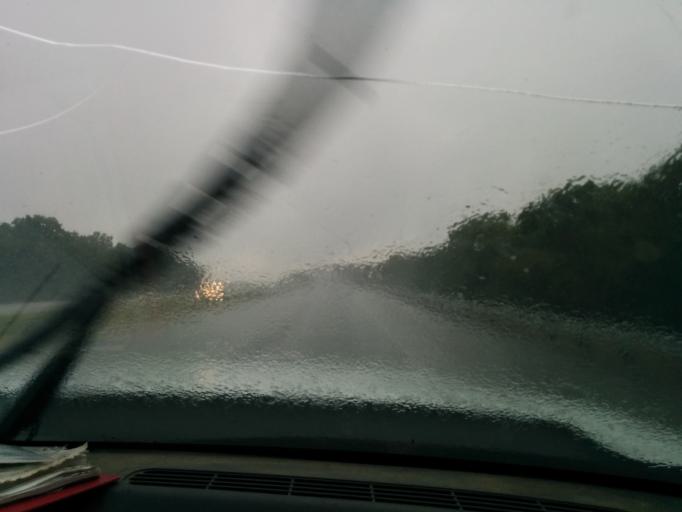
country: US
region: Oklahoma
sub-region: Okmulgee County
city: Beggs
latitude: 35.7332
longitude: -96.0046
